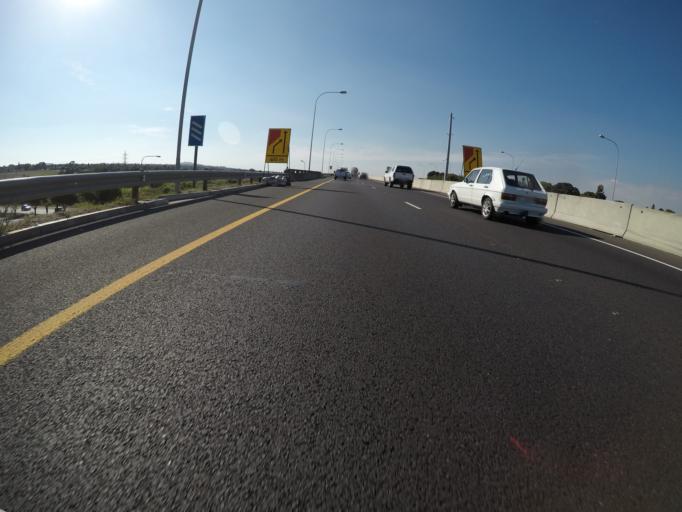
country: ZA
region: Western Cape
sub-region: City of Cape Town
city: Kraaifontein
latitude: -33.8795
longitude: 18.6730
